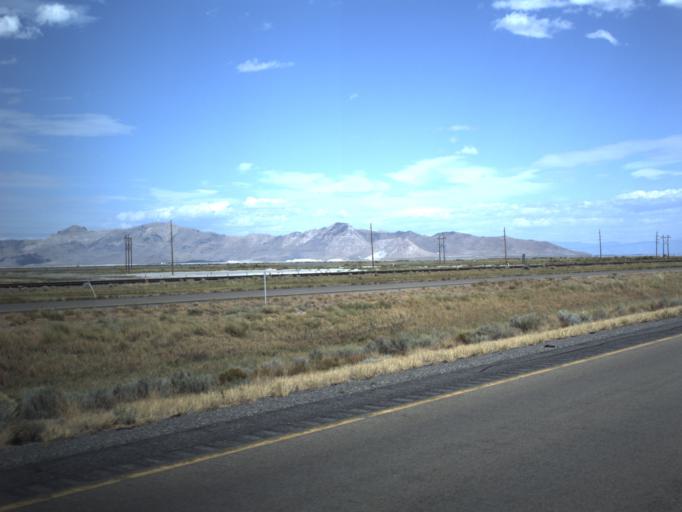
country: US
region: Utah
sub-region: Tooele County
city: Grantsville
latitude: 40.7448
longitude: -112.6429
